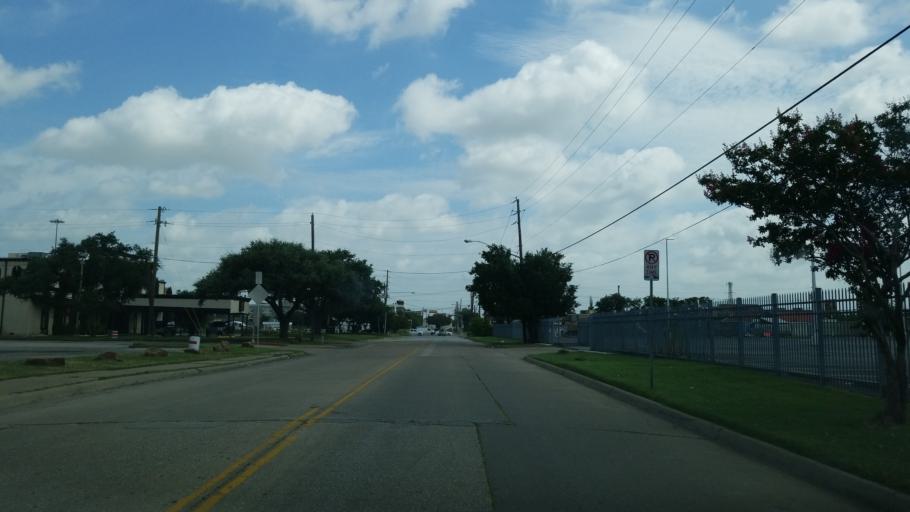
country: US
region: Texas
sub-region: Dallas County
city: Farmers Branch
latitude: 32.8792
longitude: -96.8960
